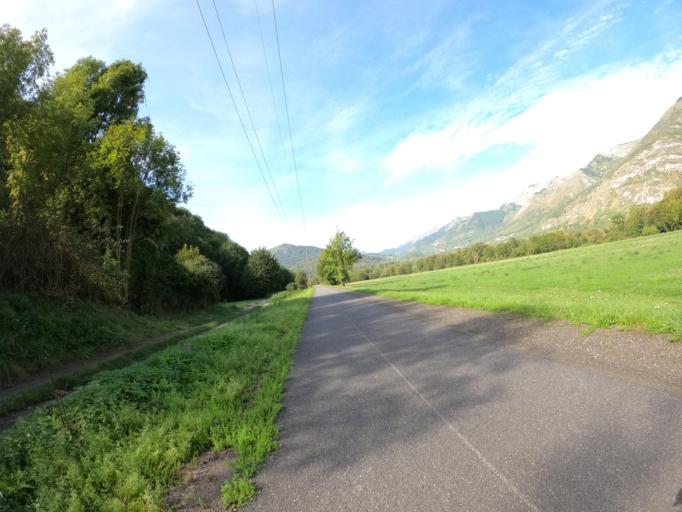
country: FR
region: Midi-Pyrenees
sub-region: Departement des Hautes-Pyrenees
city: Argeles-Gazost
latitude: 43.0236
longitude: -0.0749
